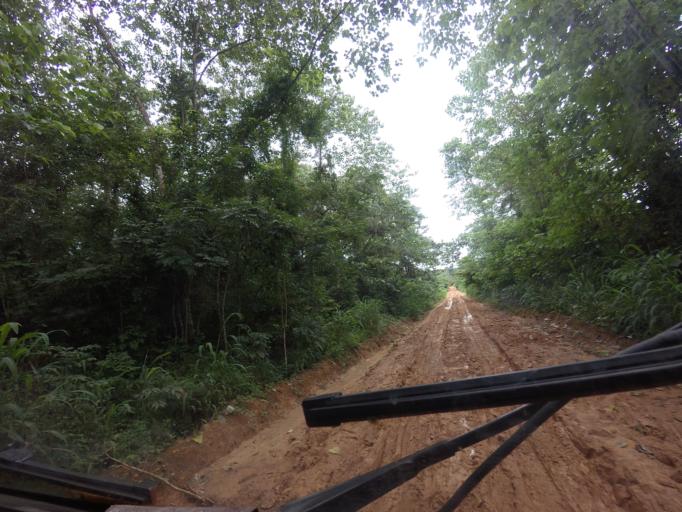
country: SL
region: Eastern Province
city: Tombodu
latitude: 8.1446
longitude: -10.6571
